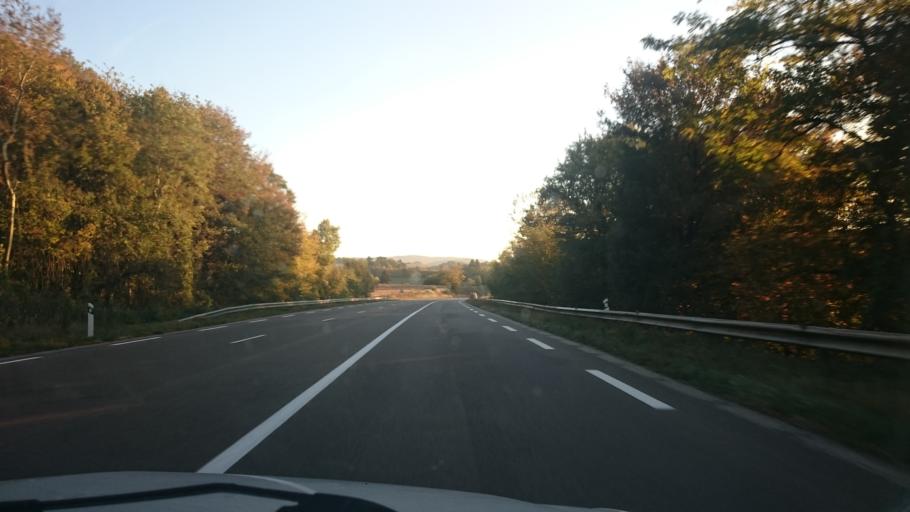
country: FR
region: Franche-Comte
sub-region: Departement du Jura
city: Mouchard
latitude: 46.9577
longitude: 5.7901
